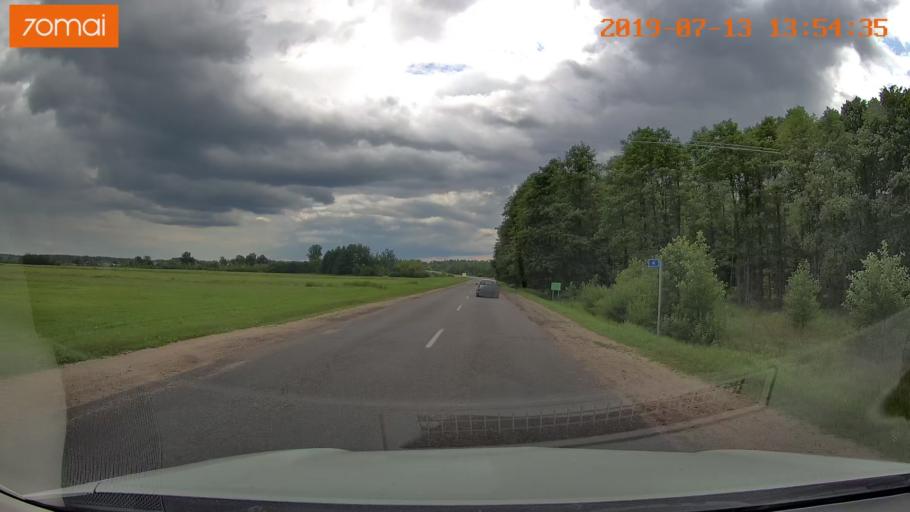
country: BY
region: Mogilev
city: Asipovichy
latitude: 53.2840
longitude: 28.6574
